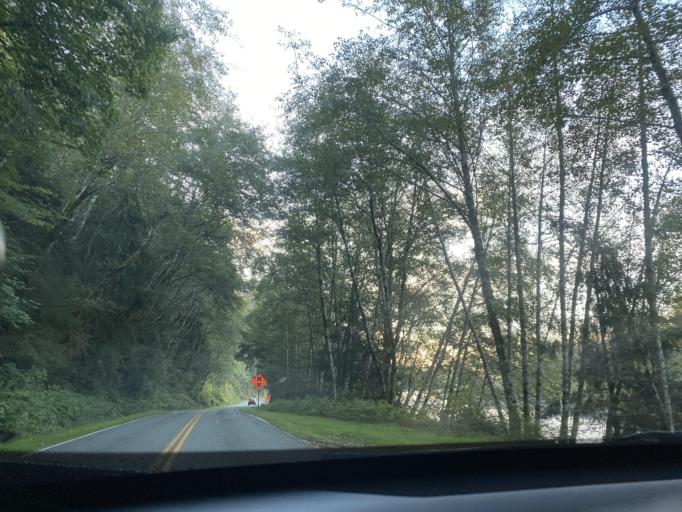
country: US
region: Washington
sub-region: Clallam County
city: Forks
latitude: 47.8229
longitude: -124.1858
